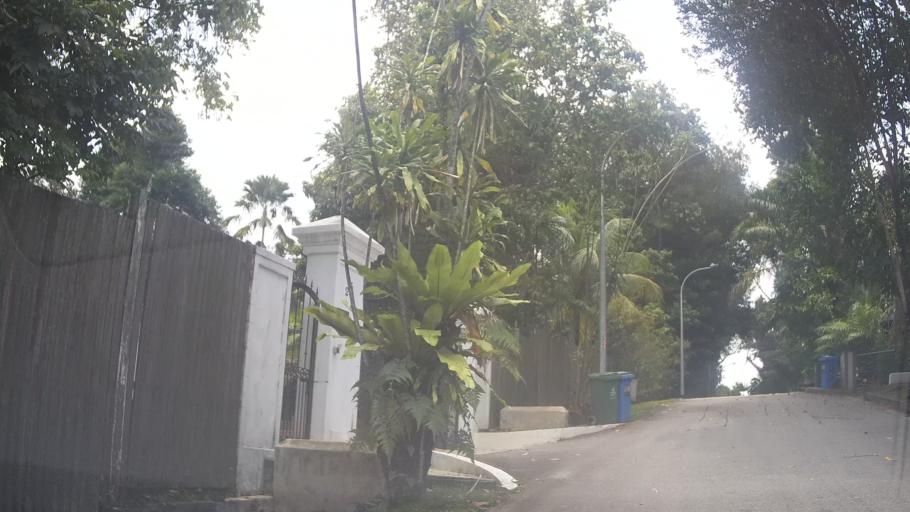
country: SG
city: Singapore
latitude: 1.3396
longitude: 103.7824
